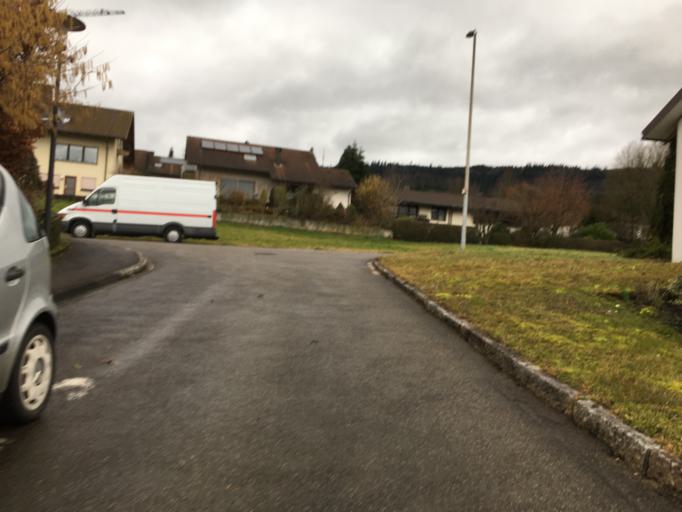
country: DE
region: Baden-Wuerttemberg
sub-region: Freiburg Region
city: Bad Sackingen
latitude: 47.5603
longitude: 7.9521
